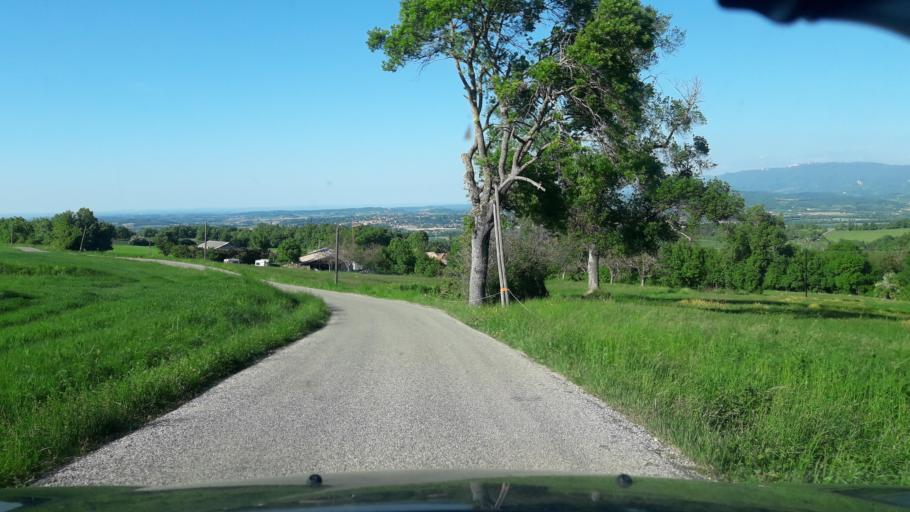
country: FR
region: Rhone-Alpes
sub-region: Departement de la Drome
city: Grane
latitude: 44.7201
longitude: 4.8919
